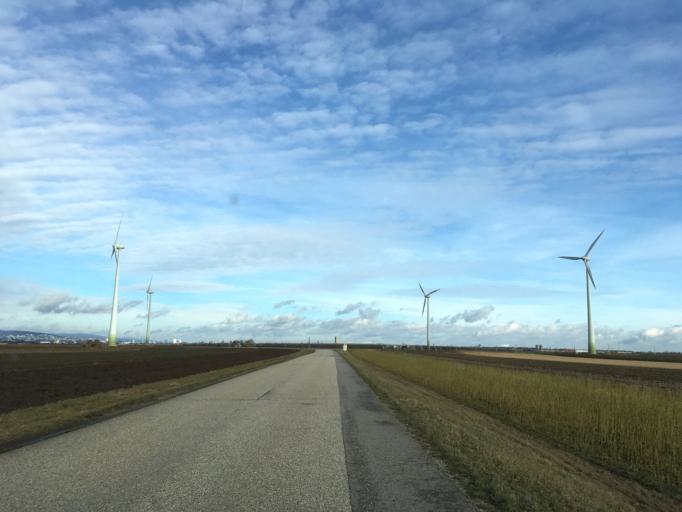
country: AT
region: Burgenland
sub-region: Politischer Bezirk Neusiedl am See
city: Pama
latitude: 48.0659
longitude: 17.0503
